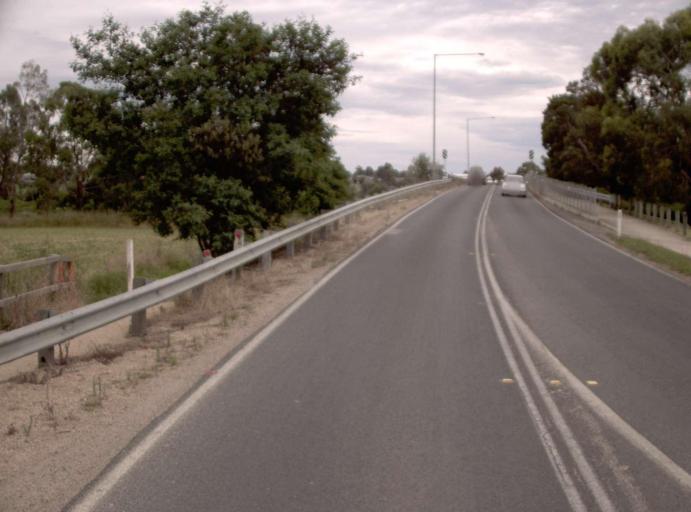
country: AU
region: Victoria
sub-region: East Gippsland
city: Bairnsdale
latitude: -37.8152
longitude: 147.6172
